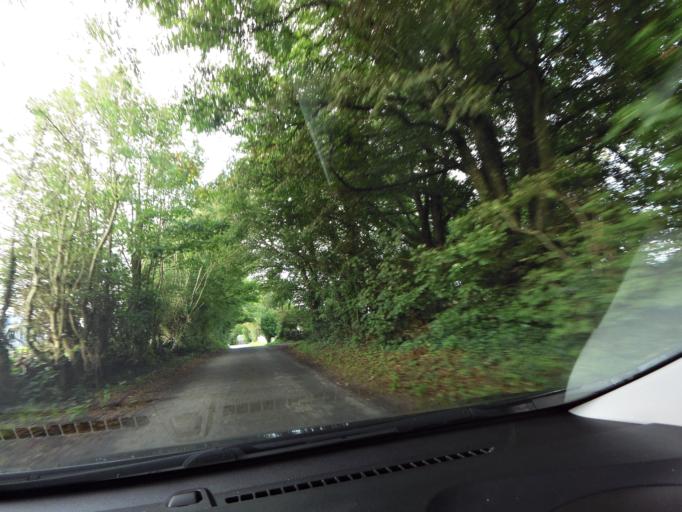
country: IE
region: Connaught
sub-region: County Galway
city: Ballinasloe
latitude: 53.3153
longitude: -8.1055
